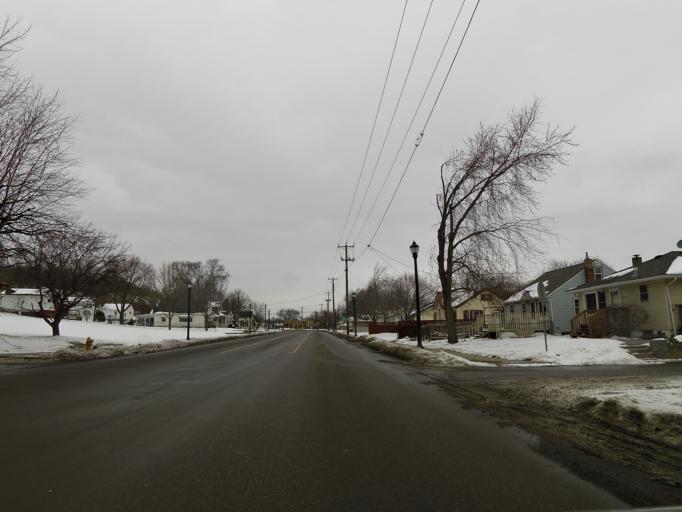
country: US
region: Minnesota
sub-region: Washington County
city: Newport
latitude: 44.8650
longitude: -93.0237
